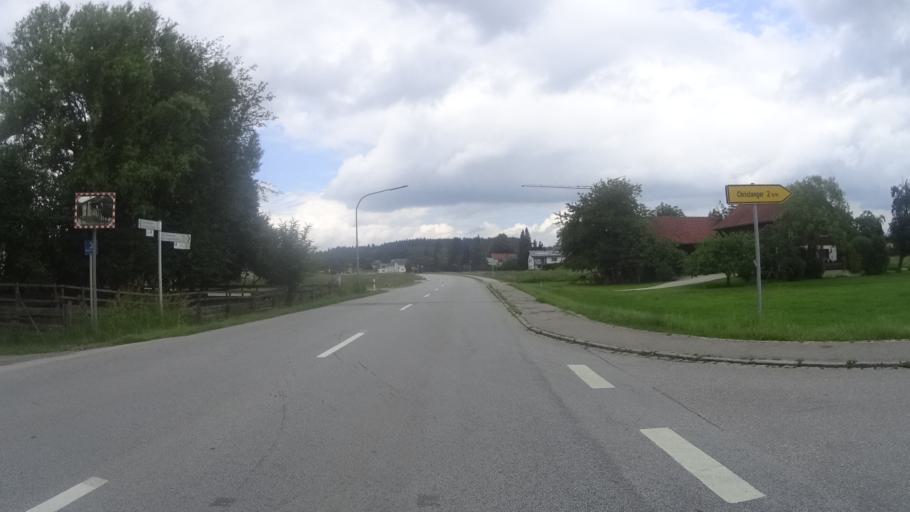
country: DE
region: Bavaria
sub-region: Lower Bavaria
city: Postmunster
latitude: 48.4223
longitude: 12.9049
